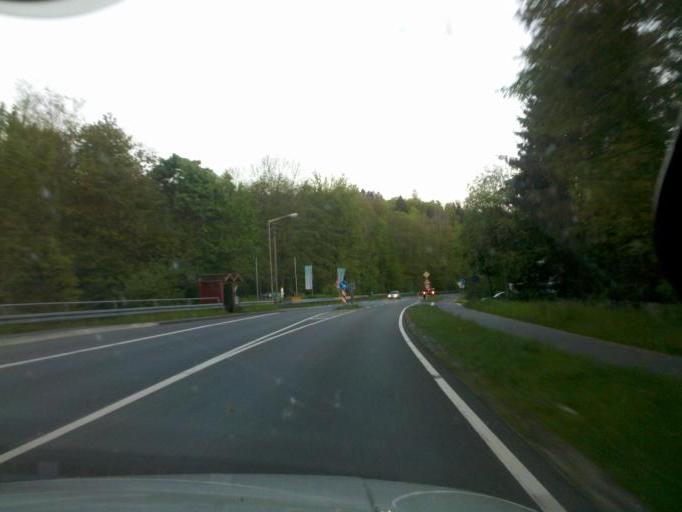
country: DE
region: North Rhine-Westphalia
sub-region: Regierungsbezirk Koln
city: Gummersbach
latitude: 51.0068
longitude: 7.5578
